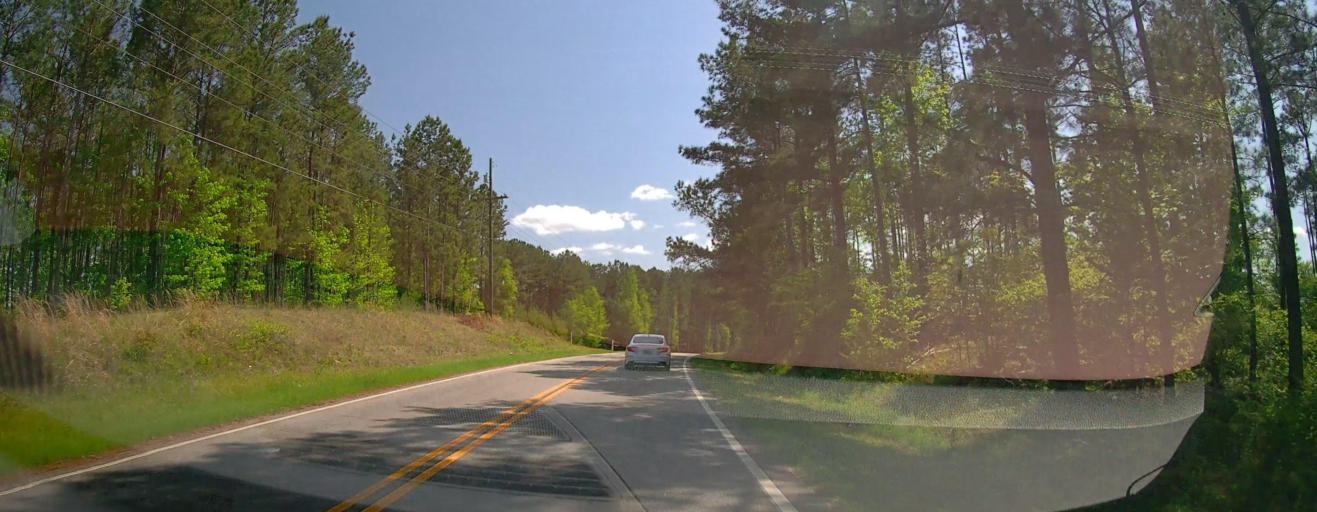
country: US
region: Georgia
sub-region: Putnam County
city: Eatonton
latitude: 33.2479
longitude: -83.3035
